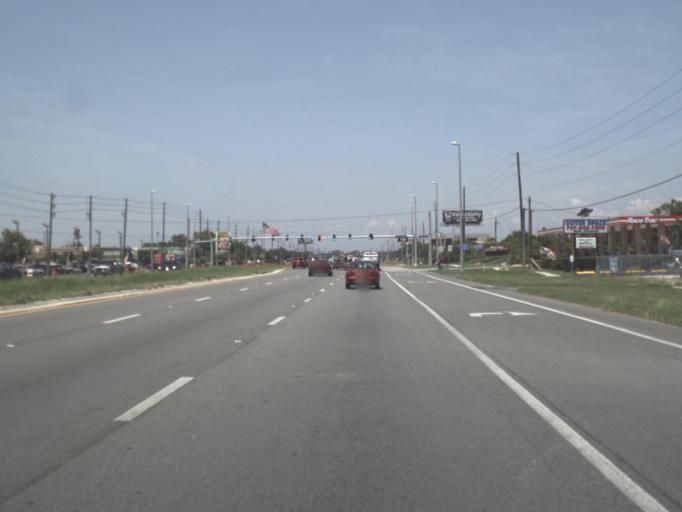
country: US
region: Florida
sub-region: Pasco County
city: Jasmine Estates
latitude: 28.3004
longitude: -82.7051
